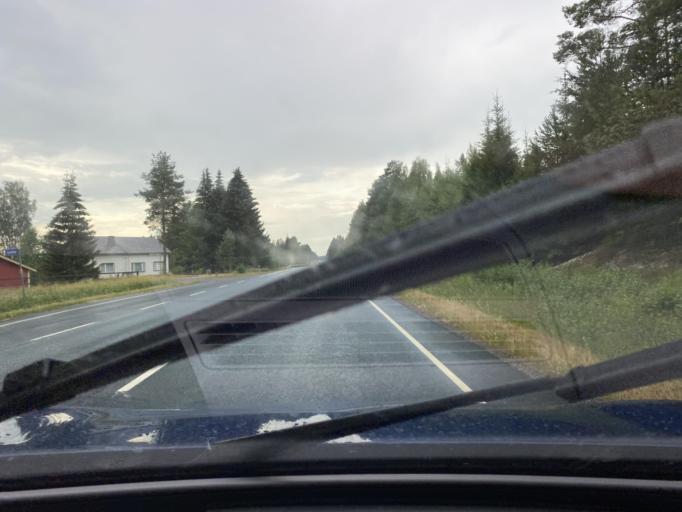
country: FI
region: Central Ostrobothnia
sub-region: Kaustinen
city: Veteli
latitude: 63.4179
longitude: 23.9414
